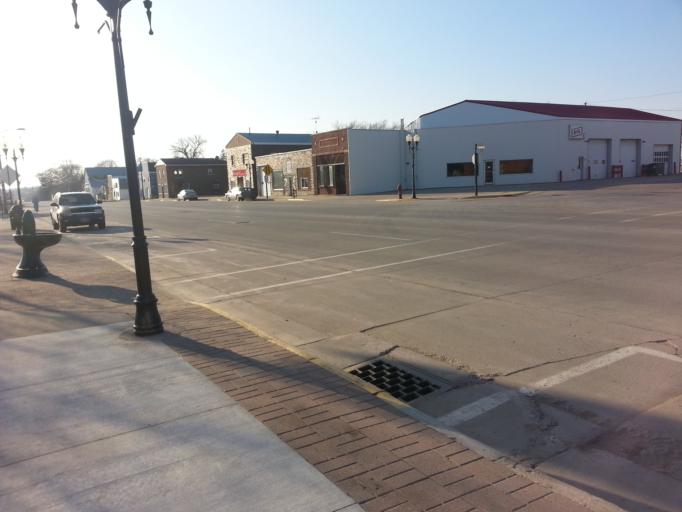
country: US
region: Iowa
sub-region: Worth County
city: Northwood
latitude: 43.4440
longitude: -93.2220
